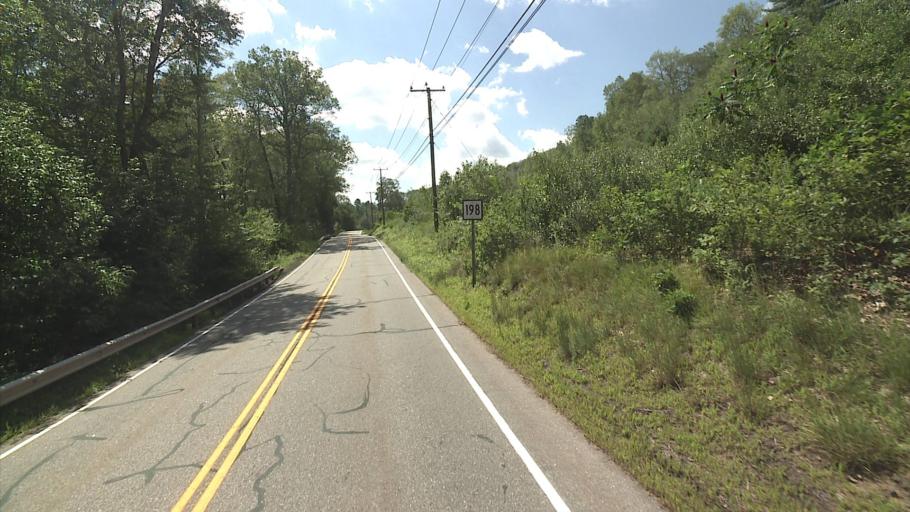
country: US
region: Connecticut
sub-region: Windham County
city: South Woodstock
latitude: 41.8916
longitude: -72.0798
